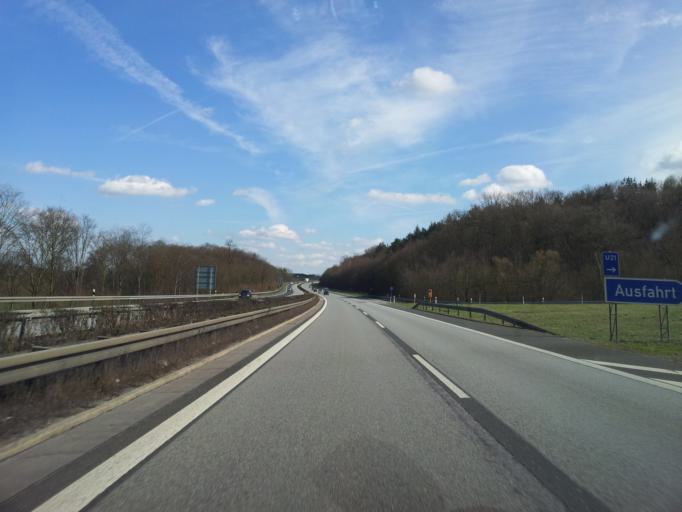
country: DE
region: Bavaria
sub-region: Regierungsbezirk Unterfranken
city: Gadheim
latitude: 50.0209
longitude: 10.3260
